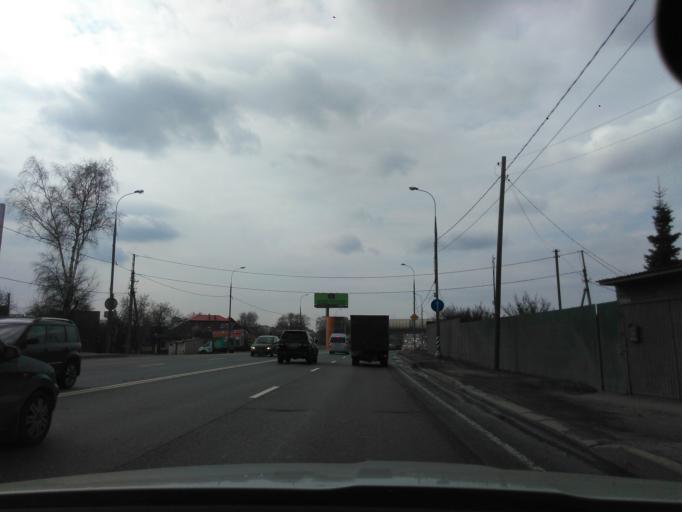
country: RU
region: Moskovskaya
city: Sheremet'yevskiy
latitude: 55.9849
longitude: 37.5292
